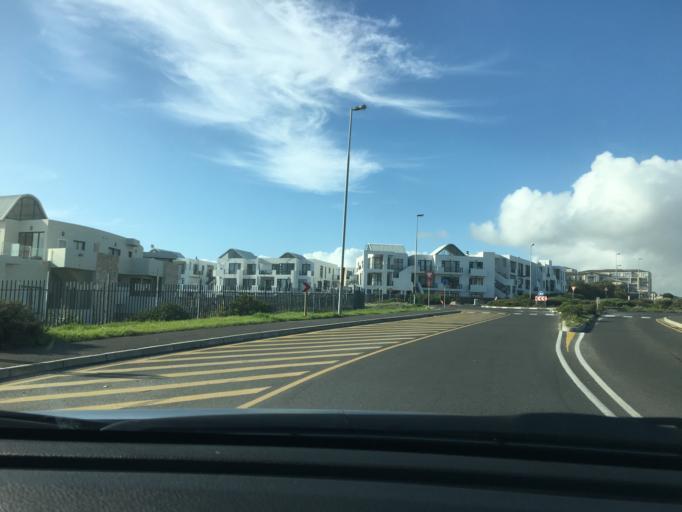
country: ZA
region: Western Cape
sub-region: City of Cape Town
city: Sunset Beach
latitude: -33.7939
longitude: 18.4589
